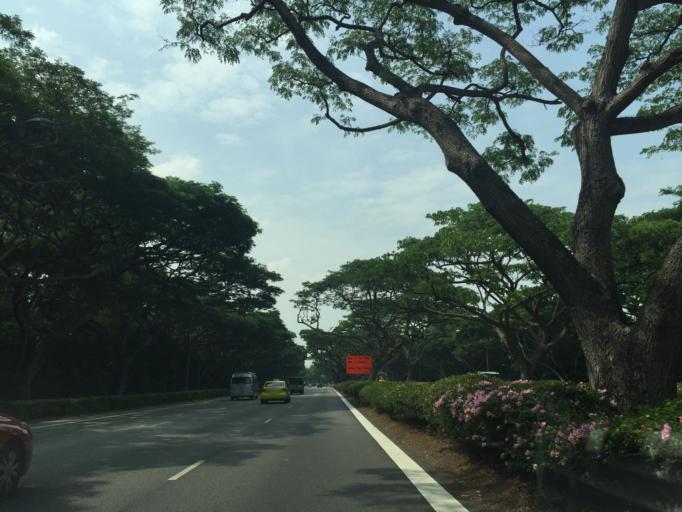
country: SG
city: Singapore
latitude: 1.3332
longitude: 103.9776
